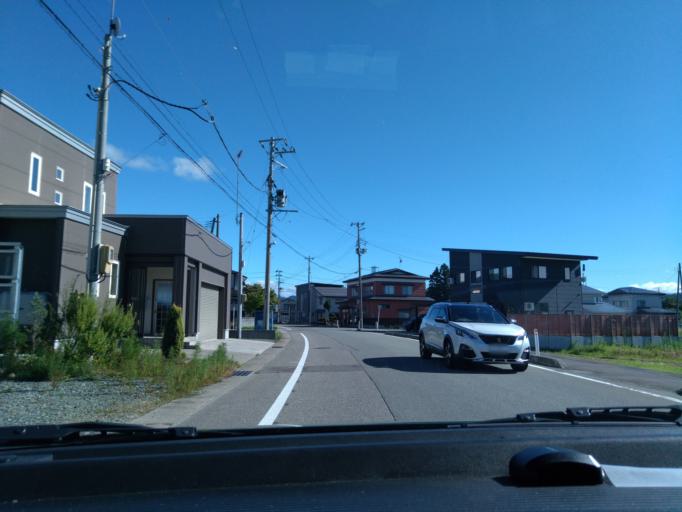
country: JP
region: Akita
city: Yuzawa
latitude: 39.2037
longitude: 140.5513
